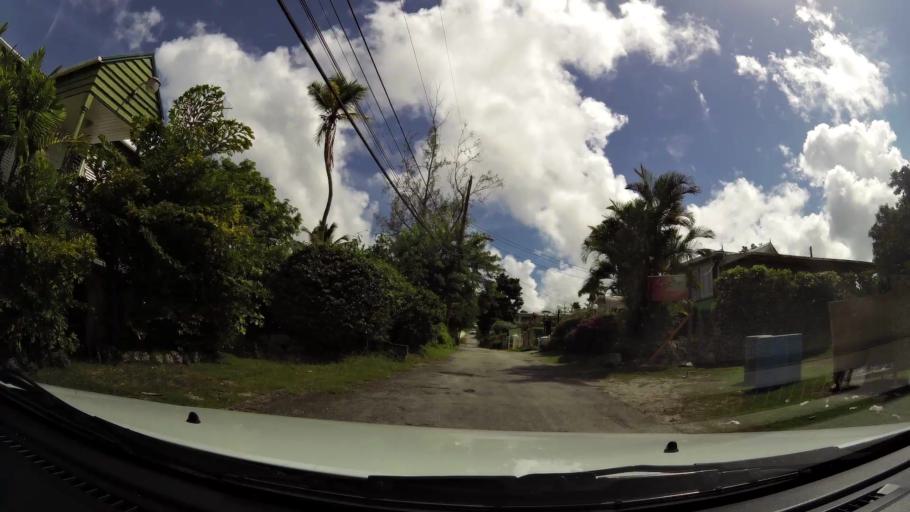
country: BB
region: Saint James
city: Holetown
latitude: 13.1561
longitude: -59.6364
